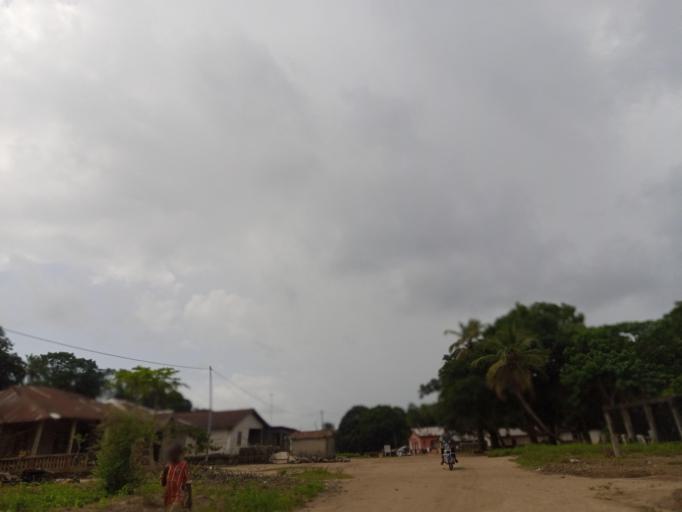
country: SL
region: Northern Province
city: Sawkta
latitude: 8.6308
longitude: -13.2025
